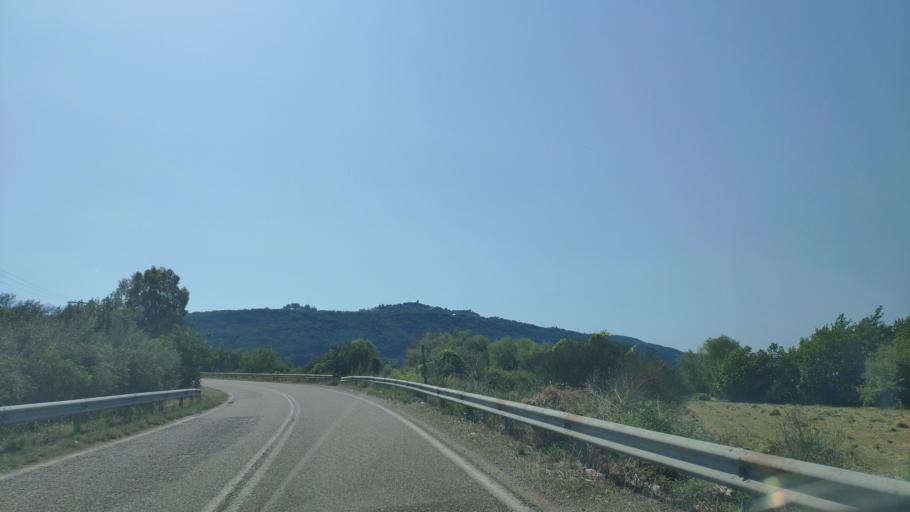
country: GR
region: West Greece
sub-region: Nomos Aitolias kai Akarnanias
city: Lepenou
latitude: 38.7069
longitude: 21.3285
